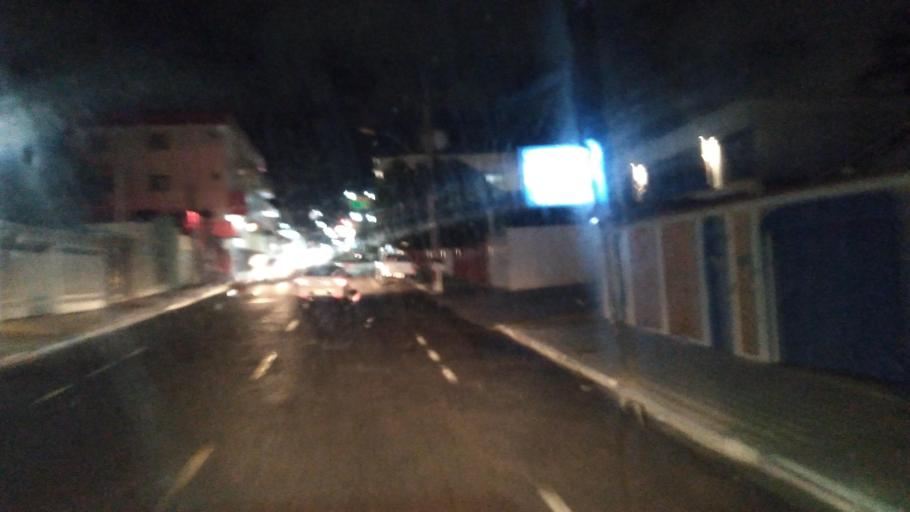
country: BR
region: Goias
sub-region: Mineiros
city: Mineiros
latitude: -17.5645
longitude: -52.5538
